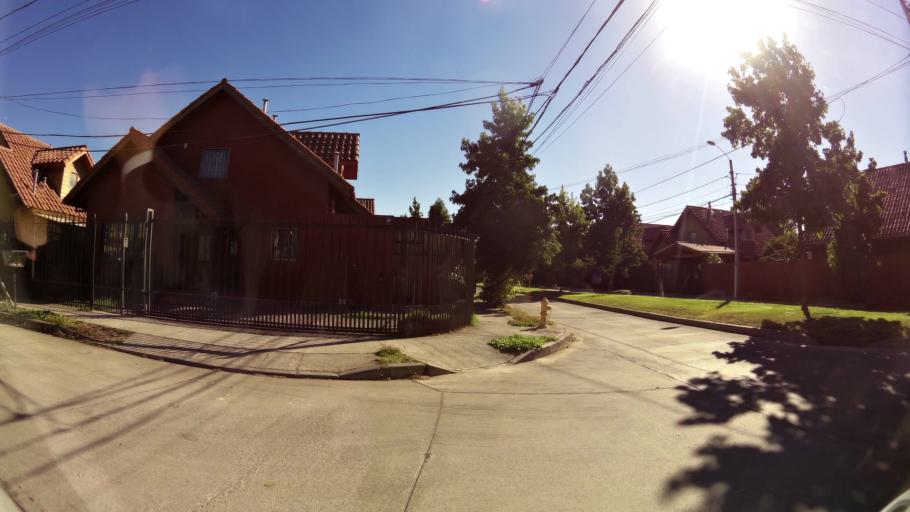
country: CL
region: O'Higgins
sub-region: Provincia de Cachapoal
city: Rancagua
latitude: -34.1937
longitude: -70.7179
